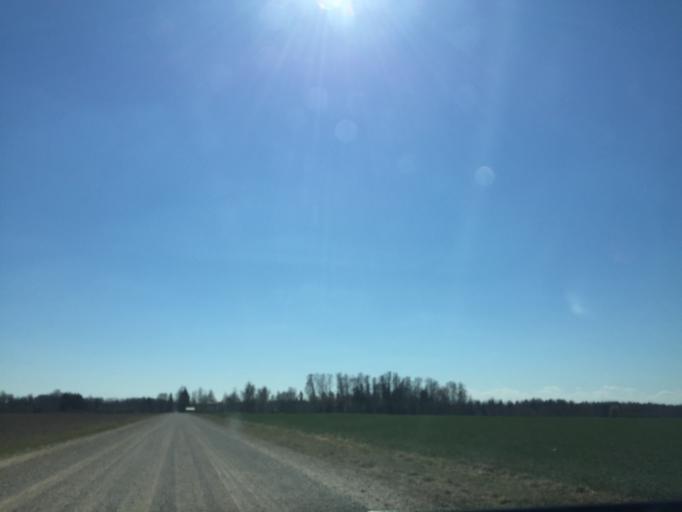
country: EE
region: Viljandimaa
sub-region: Viiratsi vald
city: Viiratsi
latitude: 58.3752
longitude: 25.7465
